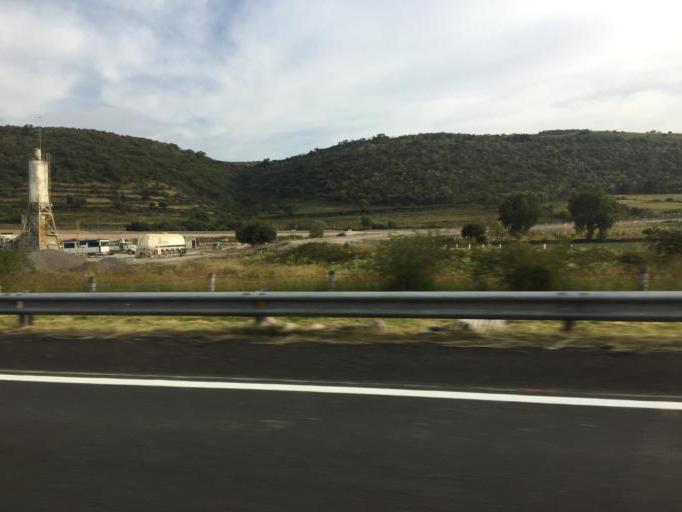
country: MX
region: Michoacan
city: Copandaro de Galeana
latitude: 19.8809
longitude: -101.2072
